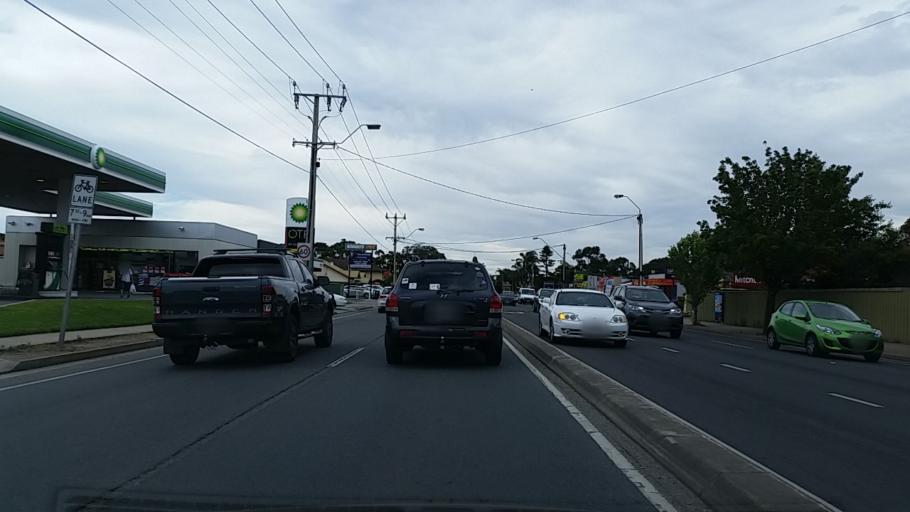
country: AU
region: South Australia
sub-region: Marion
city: Sturt
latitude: -35.0061
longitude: 138.5579
